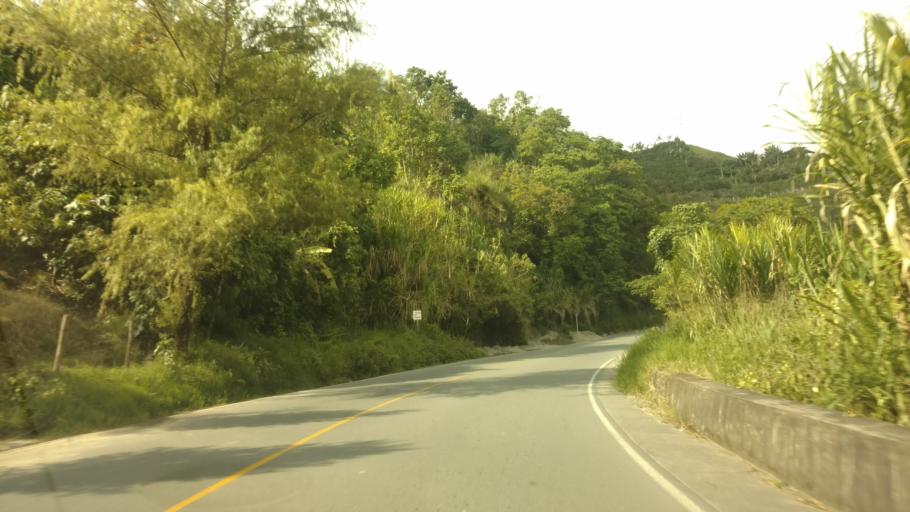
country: CO
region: Caldas
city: Neira
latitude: 5.1380
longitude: -75.4961
